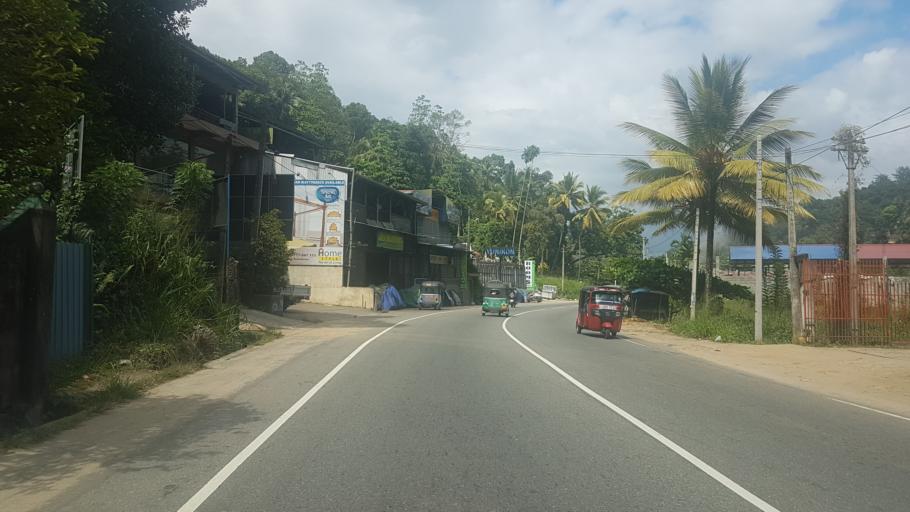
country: LK
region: Central
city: Gampola
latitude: 7.2050
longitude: 80.5991
